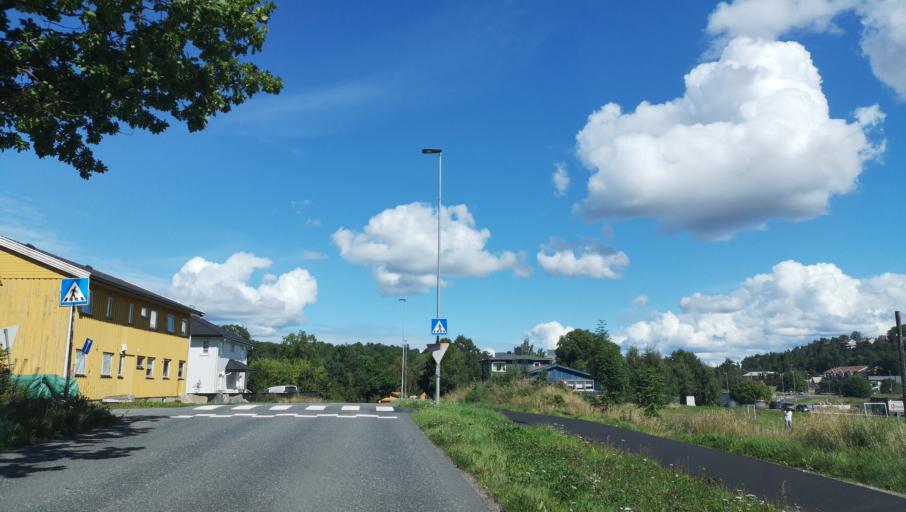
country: NO
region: Akershus
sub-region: Frogn
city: Drobak
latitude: 59.6650
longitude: 10.6407
